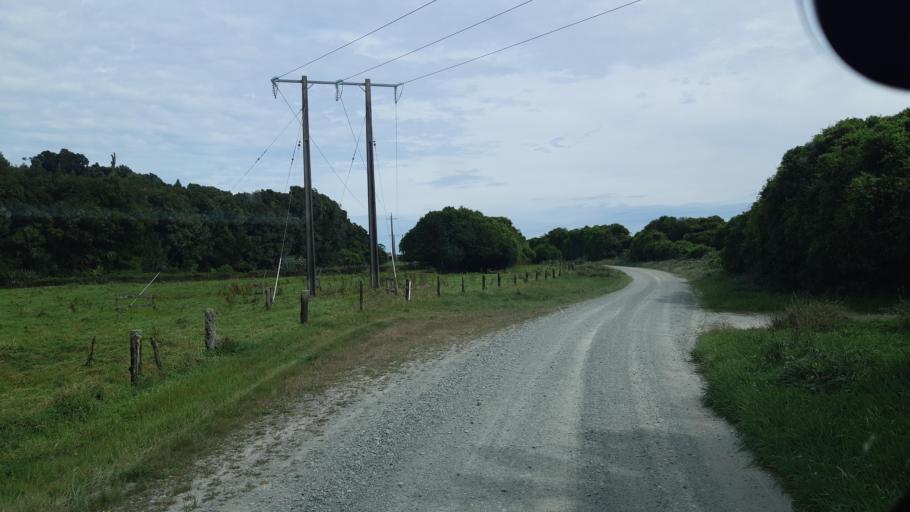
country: NZ
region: West Coast
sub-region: Westland District
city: Hokitika
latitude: -42.9085
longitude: 170.7623
